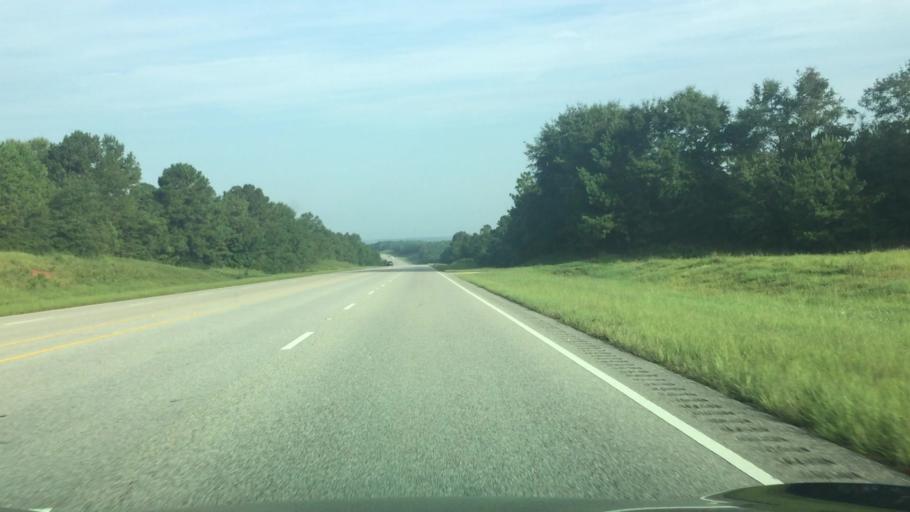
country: US
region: Alabama
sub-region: Covington County
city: Andalusia
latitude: 31.4540
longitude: -86.6320
